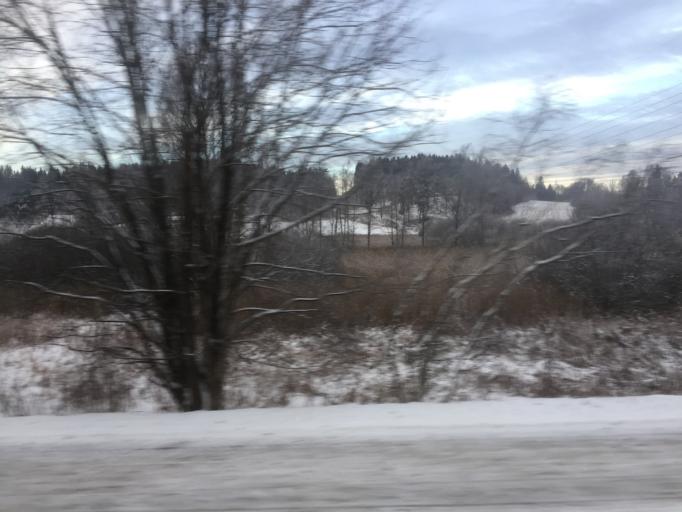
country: NO
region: Akershus
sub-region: As
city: As
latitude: 59.7339
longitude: 10.7435
